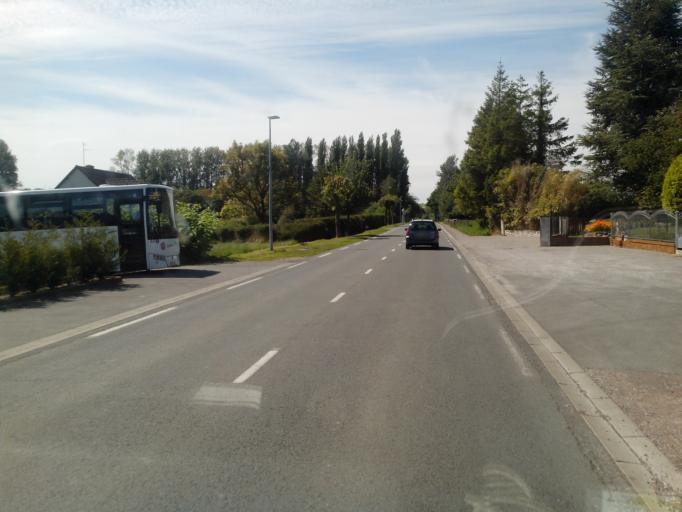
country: FR
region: Nord-Pas-de-Calais
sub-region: Departement du Pas-de-Calais
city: Montreuil
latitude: 50.4930
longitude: 1.7171
